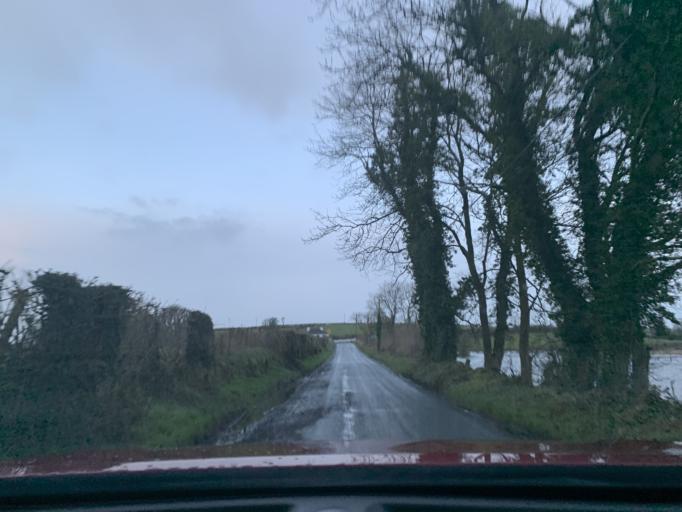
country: IE
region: Connaught
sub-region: Sligo
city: Ballymote
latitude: 54.0449
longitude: -8.6083
